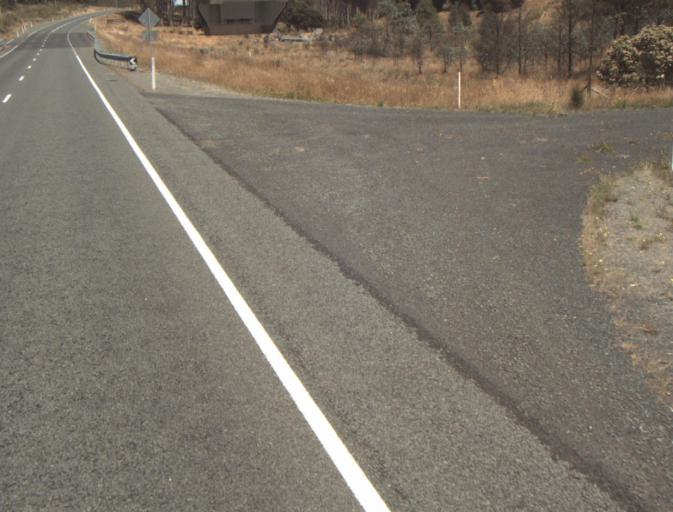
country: AU
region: Tasmania
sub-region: Launceston
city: Newstead
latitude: -41.3408
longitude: 147.3464
